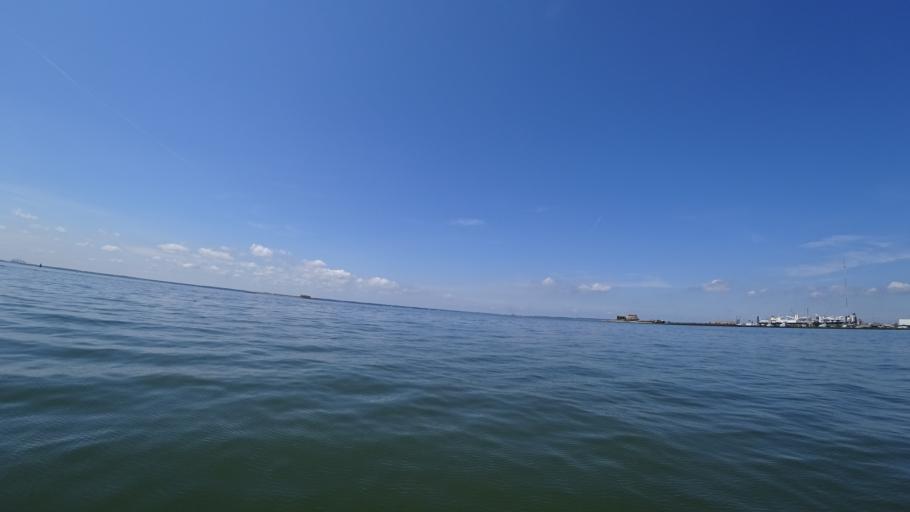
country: US
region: Virginia
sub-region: City of Newport News
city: Newport News
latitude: 36.9640
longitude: -76.4012
